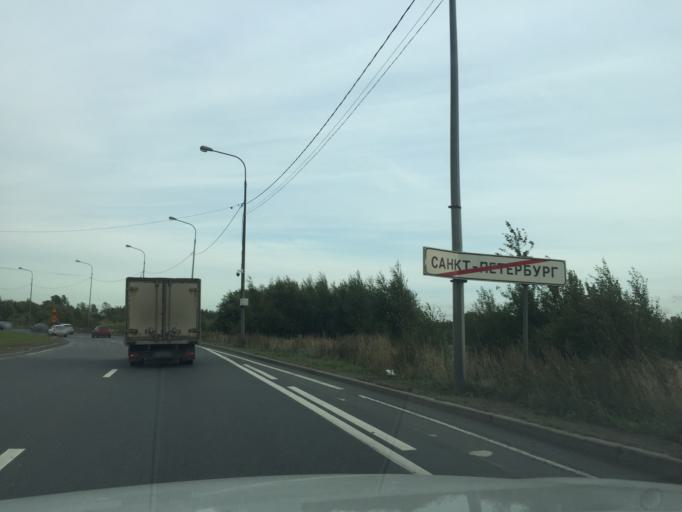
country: RU
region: St.-Petersburg
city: Krasnogvargeisky
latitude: 59.9874
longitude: 30.4672
